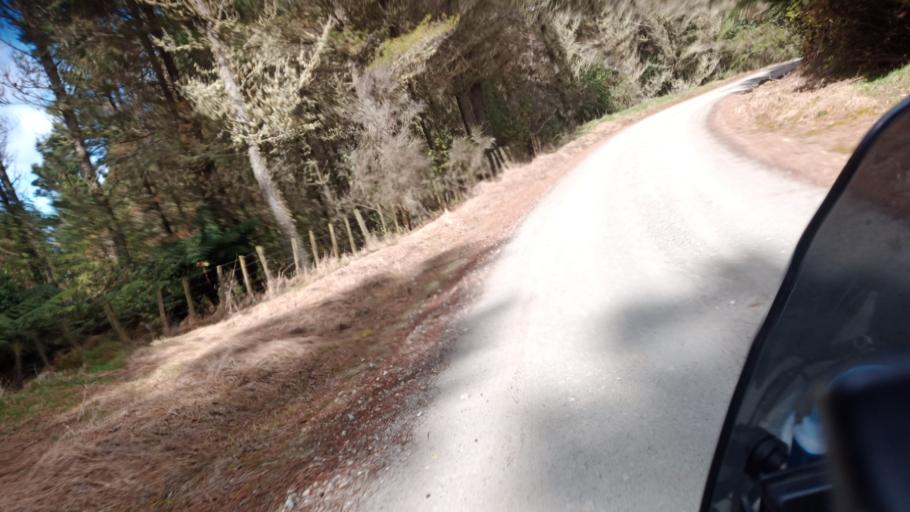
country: NZ
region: Gisborne
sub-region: Gisborne District
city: Gisborne
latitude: -38.8568
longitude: 177.7967
